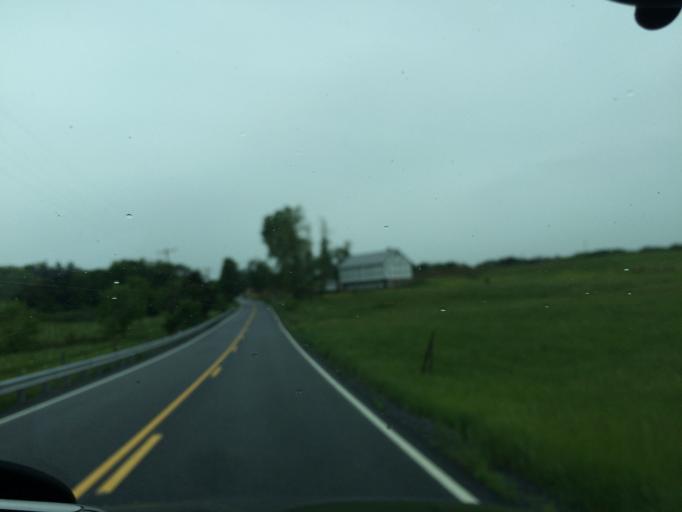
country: US
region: Maryland
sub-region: Frederick County
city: Woodsboro
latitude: 39.6071
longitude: -77.3061
